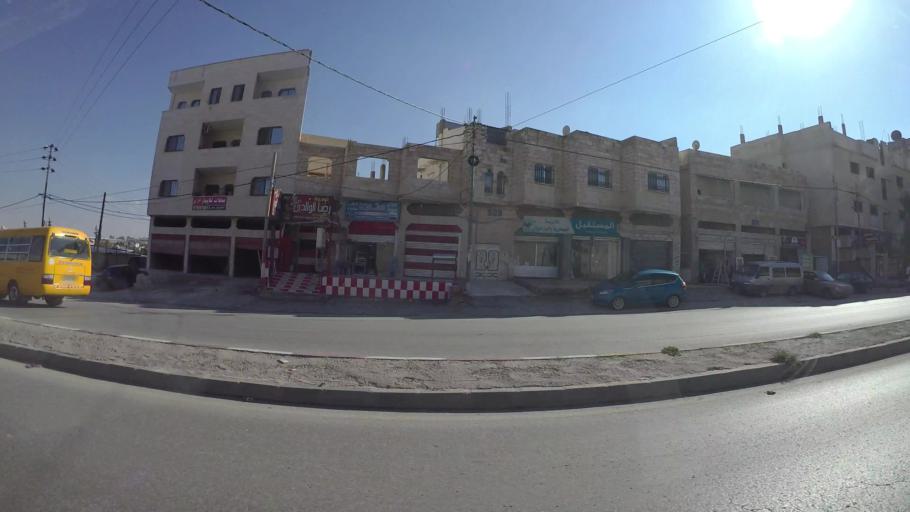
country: JO
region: Zarqa
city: Russeifa
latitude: 32.0211
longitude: 36.0104
